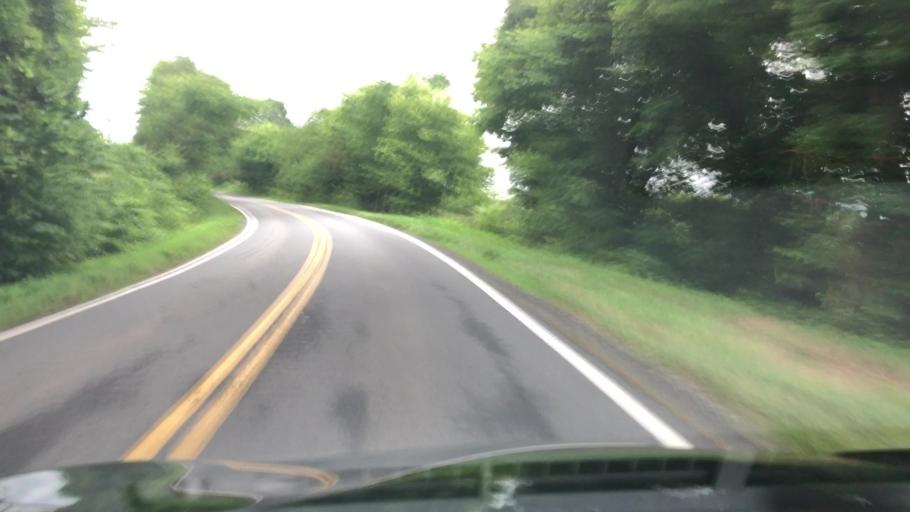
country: US
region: Virginia
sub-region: Prince William County
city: Nokesville
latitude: 38.6102
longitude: -77.6065
